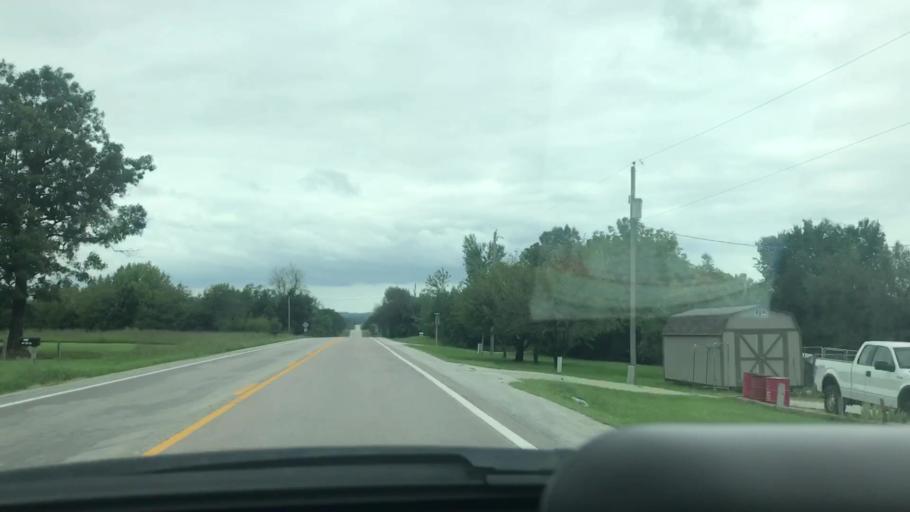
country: US
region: Missouri
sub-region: Dallas County
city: Buffalo
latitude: 37.7060
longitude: -93.1112
